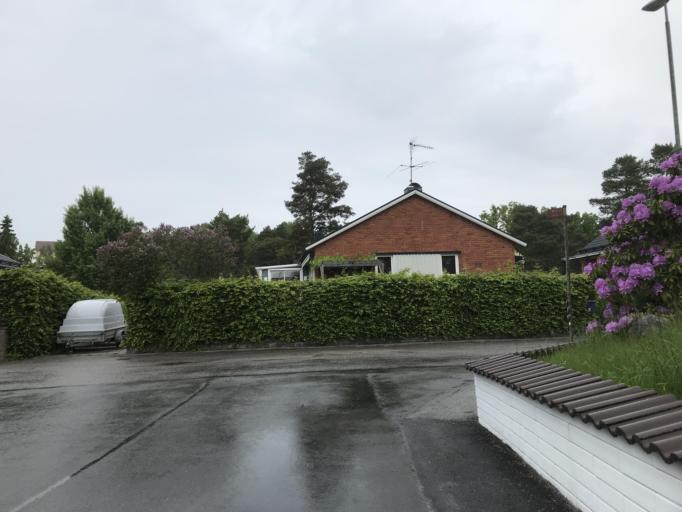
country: SE
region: Stockholm
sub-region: Huddinge Kommun
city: Huddinge
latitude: 59.2490
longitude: 17.9749
